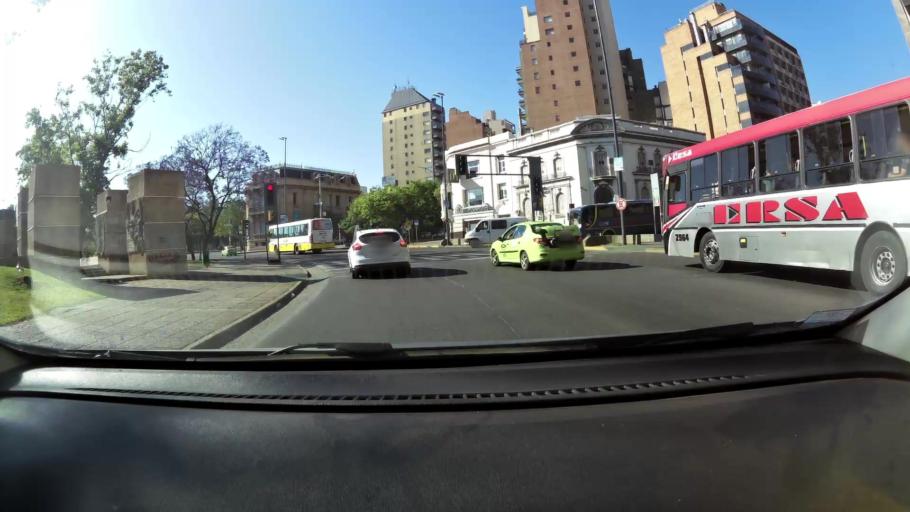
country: AR
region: Cordoba
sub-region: Departamento de Capital
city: Cordoba
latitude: -31.4287
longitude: -64.1853
